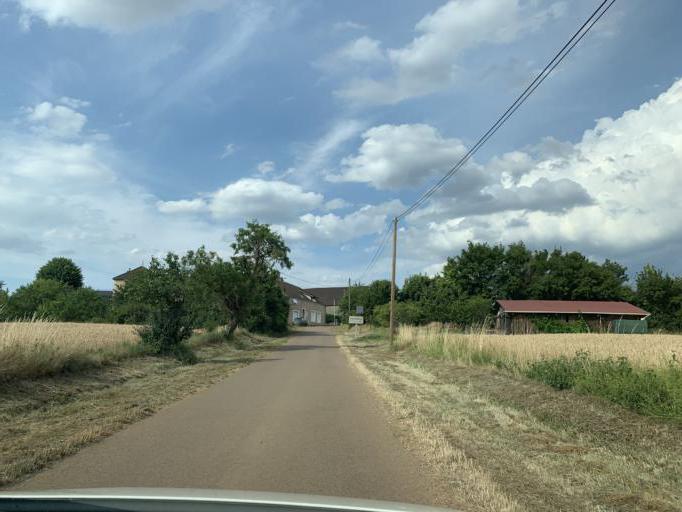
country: FR
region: Bourgogne
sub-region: Departement de l'Yonne
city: Fontenailles
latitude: 47.4956
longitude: 3.4300
